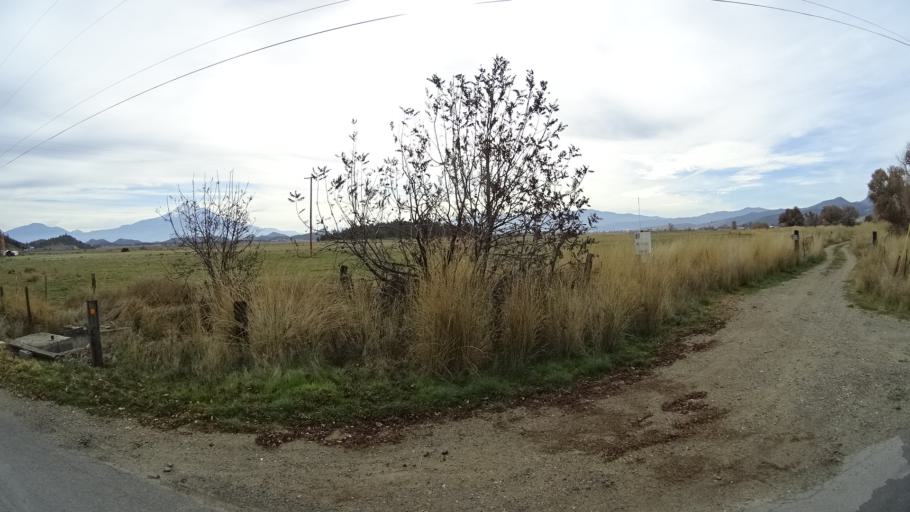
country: US
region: California
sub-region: Siskiyou County
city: Montague
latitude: 41.6583
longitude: -122.5108
